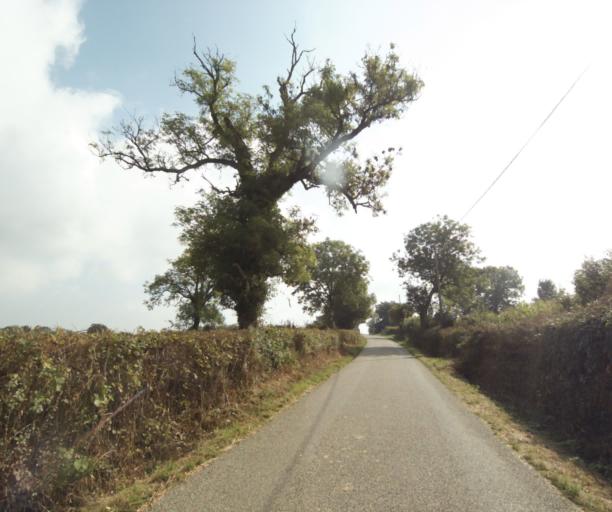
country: FR
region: Bourgogne
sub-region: Departement de Saone-et-Loire
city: Charolles
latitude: 46.4276
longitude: 4.2902
